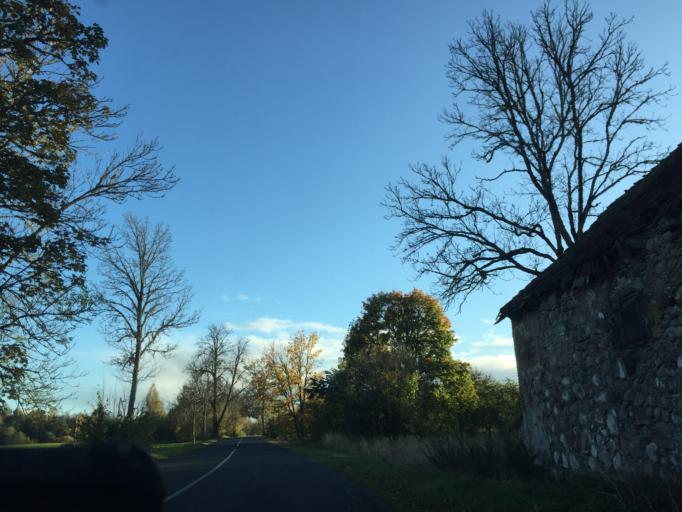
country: LV
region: Broceni
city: Broceni
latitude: 56.8522
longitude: 22.3867
